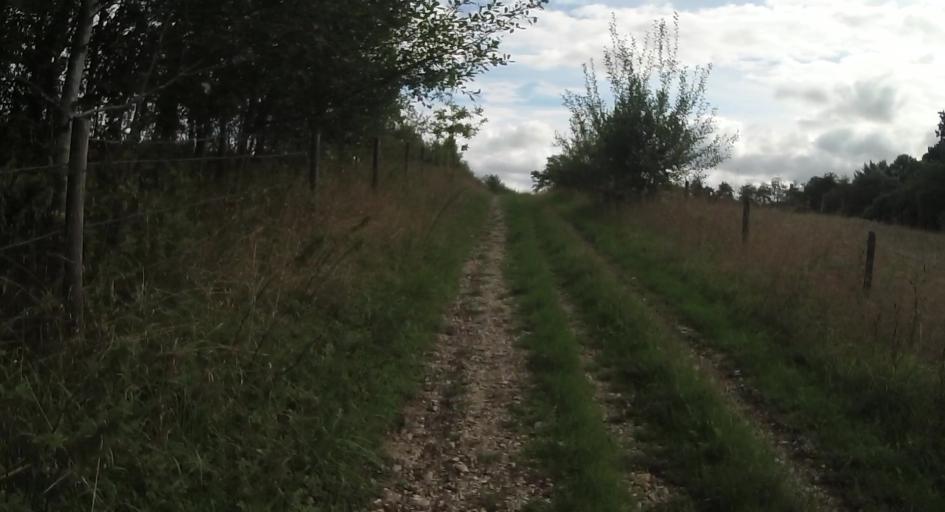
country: GB
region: England
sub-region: West Berkshire
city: Thatcham
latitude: 51.3842
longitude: -1.2398
